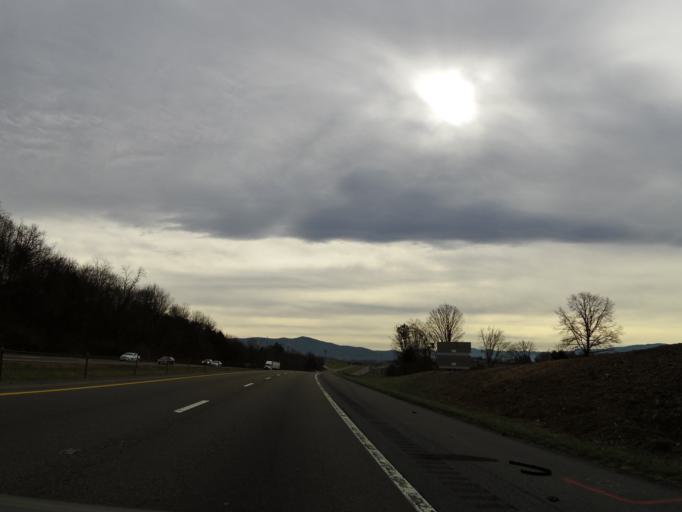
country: US
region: Tennessee
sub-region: Cocke County
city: Newport
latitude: 35.9558
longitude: -83.2072
